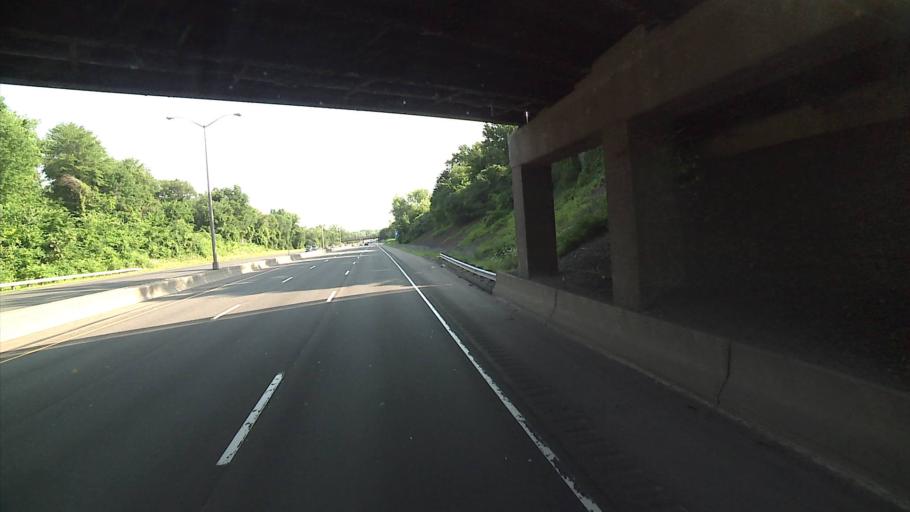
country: US
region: Connecticut
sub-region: Hartford County
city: Windsor Locks
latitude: 41.9385
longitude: -72.6070
